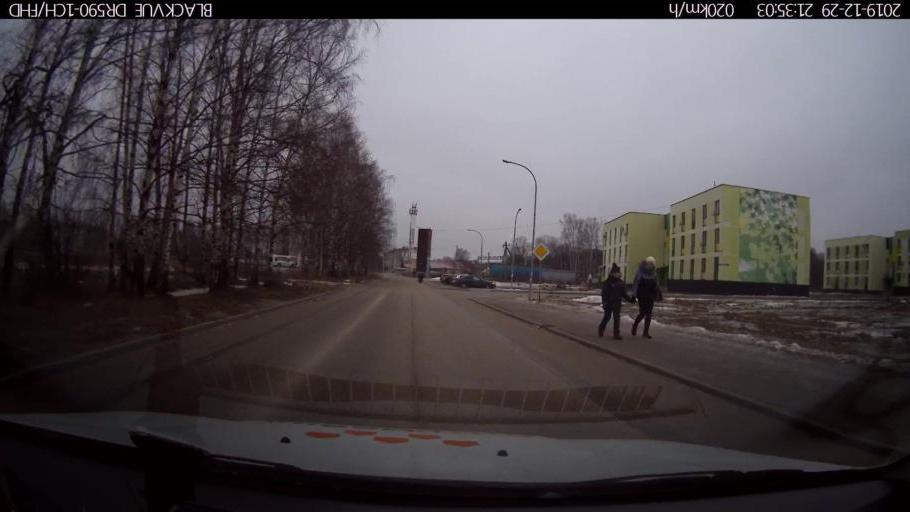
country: RU
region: Nizjnij Novgorod
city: Afonino
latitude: 56.2135
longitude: 44.0254
